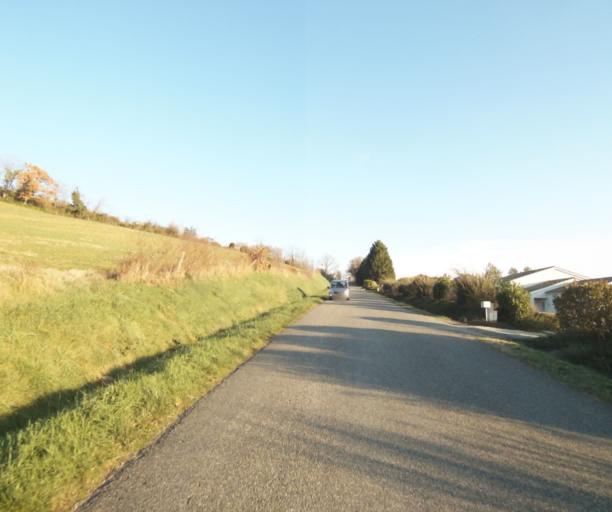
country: FR
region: Midi-Pyrenees
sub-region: Departement du Tarn-et-Garonne
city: Moissac
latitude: 44.1227
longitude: 1.1203
